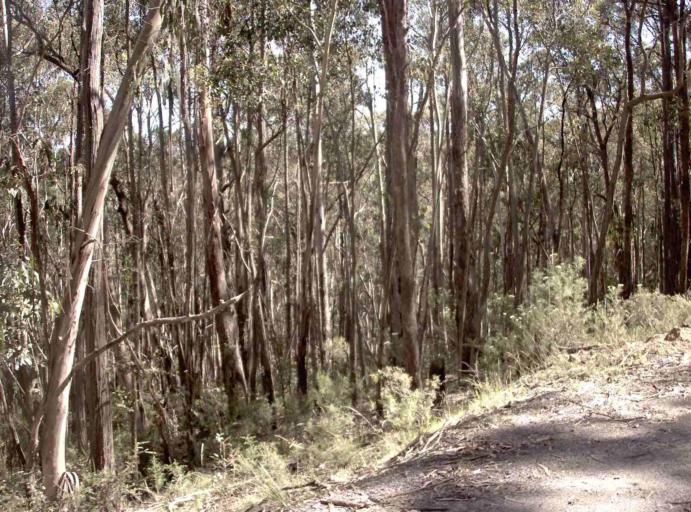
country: AU
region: New South Wales
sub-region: Bombala
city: Bombala
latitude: -37.2672
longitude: 148.7230
